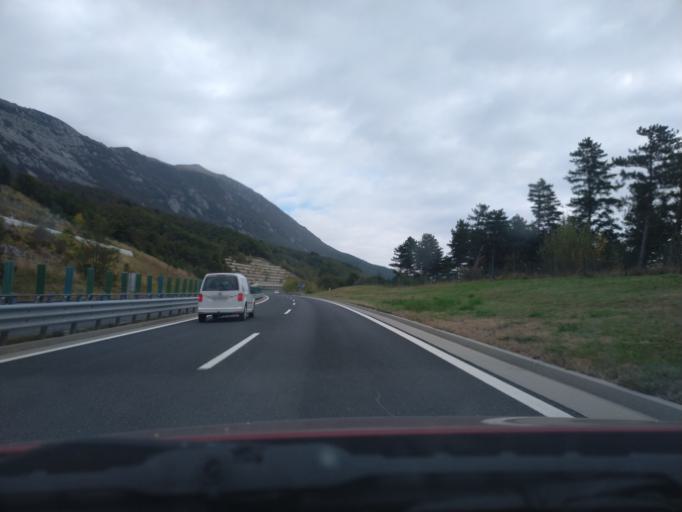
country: SI
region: Vipava
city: Vipava
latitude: 45.7849
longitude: 14.0056
